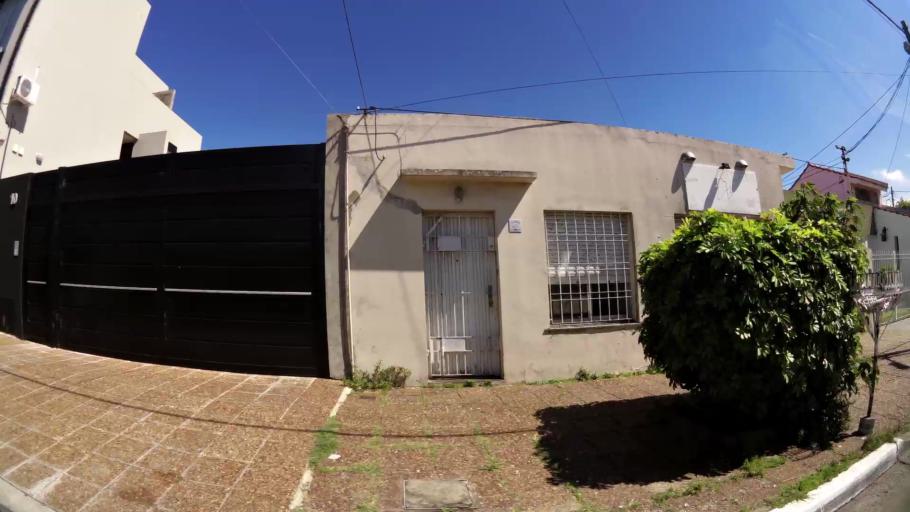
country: AR
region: Buenos Aires
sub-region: Partido de Quilmes
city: Quilmes
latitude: -34.7004
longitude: -58.2842
